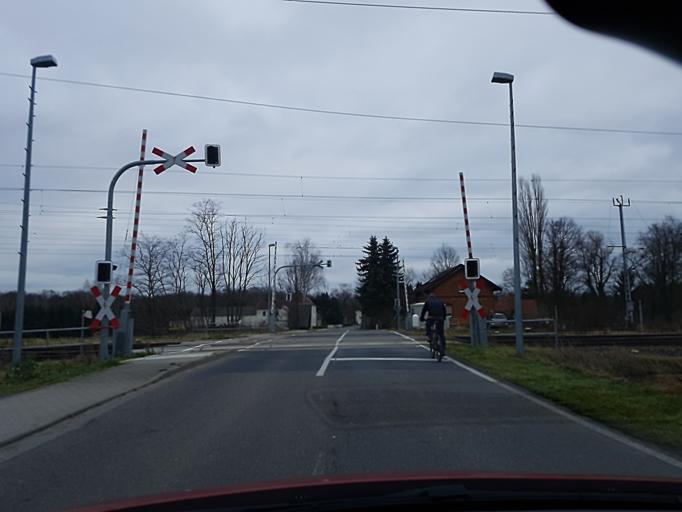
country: DE
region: Brandenburg
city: Elsterwerda
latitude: 51.4492
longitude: 13.5113
